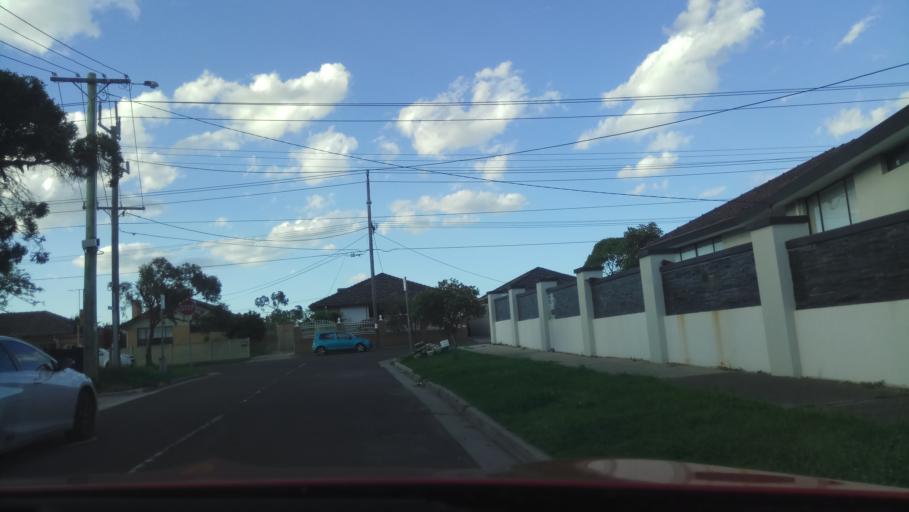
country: AU
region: Victoria
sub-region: Hobsons Bay
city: Altona North
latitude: -37.8303
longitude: 144.8366
